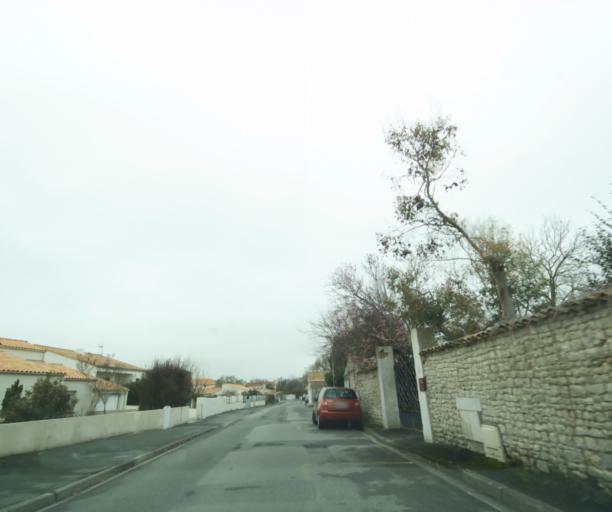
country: FR
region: Poitou-Charentes
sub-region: Departement de la Charente-Maritime
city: Lagord
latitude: 46.1829
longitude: -1.1407
